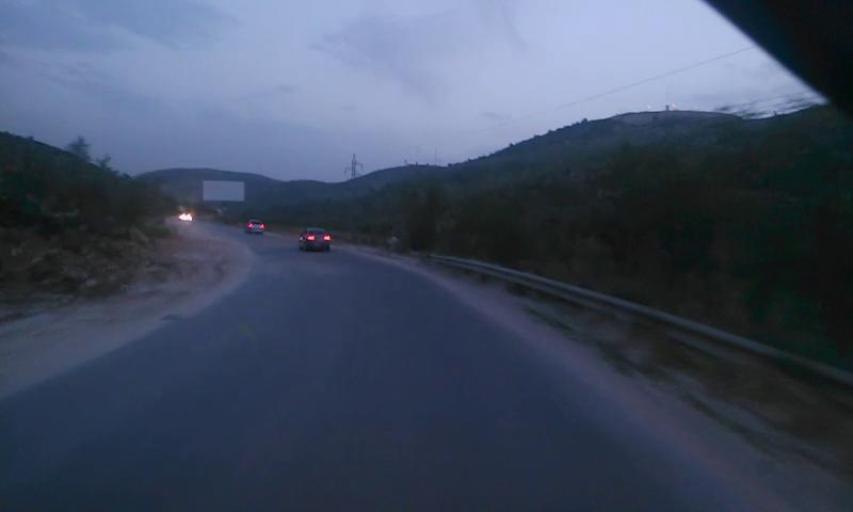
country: PS
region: West Bank
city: `Anabta
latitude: 32.2971
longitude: 35.1320
